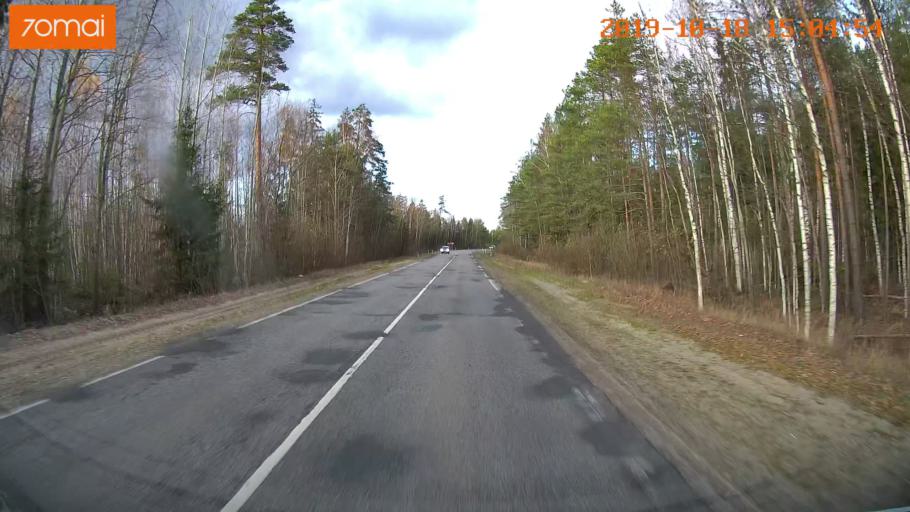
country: RU
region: Vladimir
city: Kurlovo
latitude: 55.5075
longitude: 40.5704
